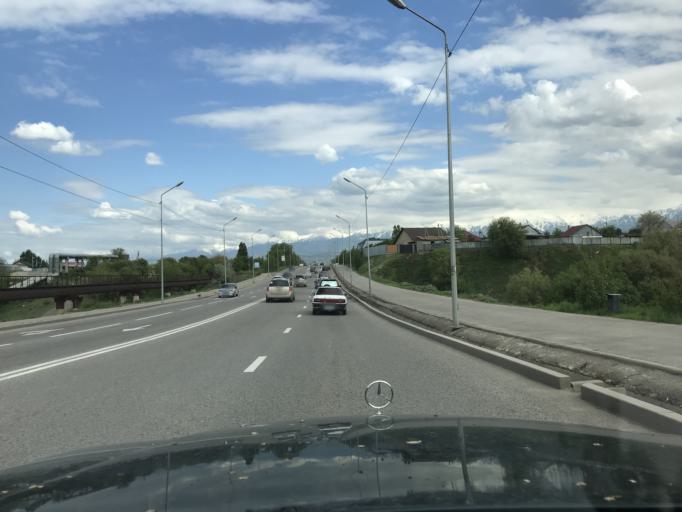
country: KZ
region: Almaty Oblysy
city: Burunday
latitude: 43.3068
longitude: 76.8793
